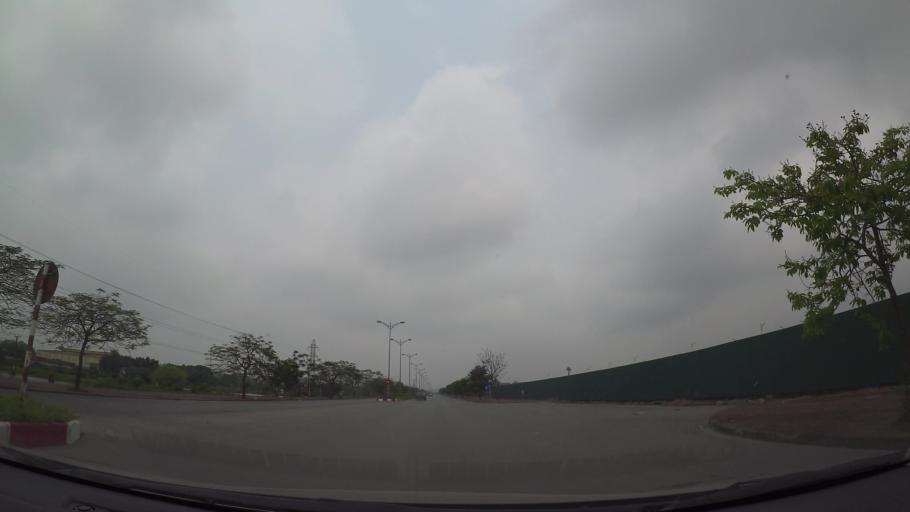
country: VN
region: Ha Noi
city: Trau Quy
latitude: 21.0346
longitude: 105.9250
